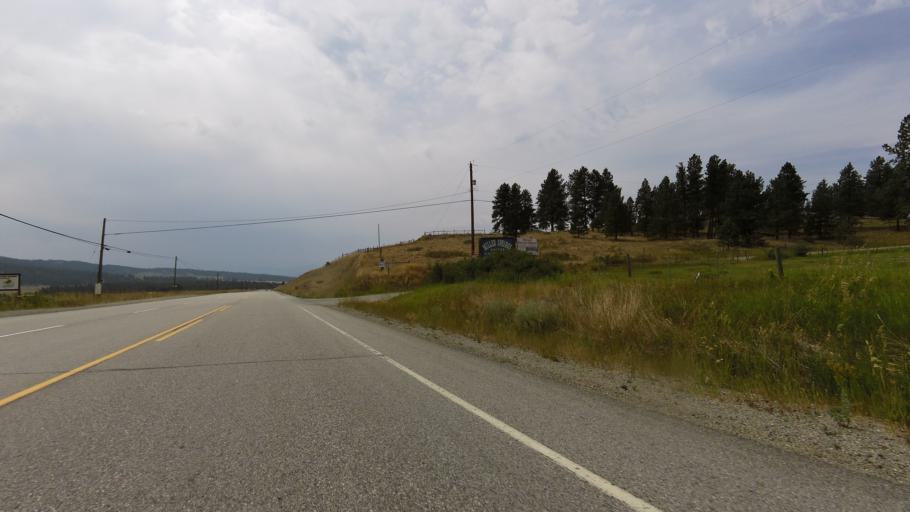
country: US
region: Washington
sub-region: Okanogan County
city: Oroville
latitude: 49.0154
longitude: -119.2208
